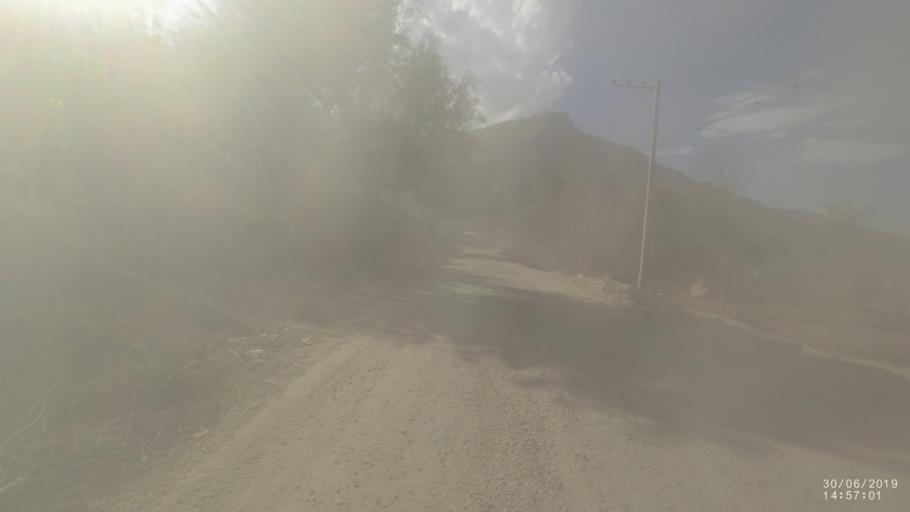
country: BO
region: Cochabamba
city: Irpa Irpa
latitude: -17.7458
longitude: -66.3540
